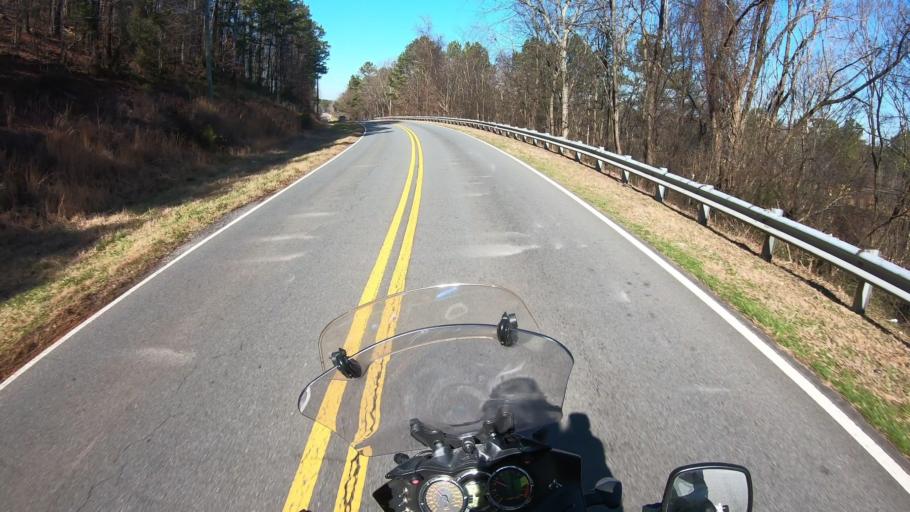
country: US
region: Georgia
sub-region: Bartow County
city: Cartersville
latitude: 34.2655
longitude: -84.8056
